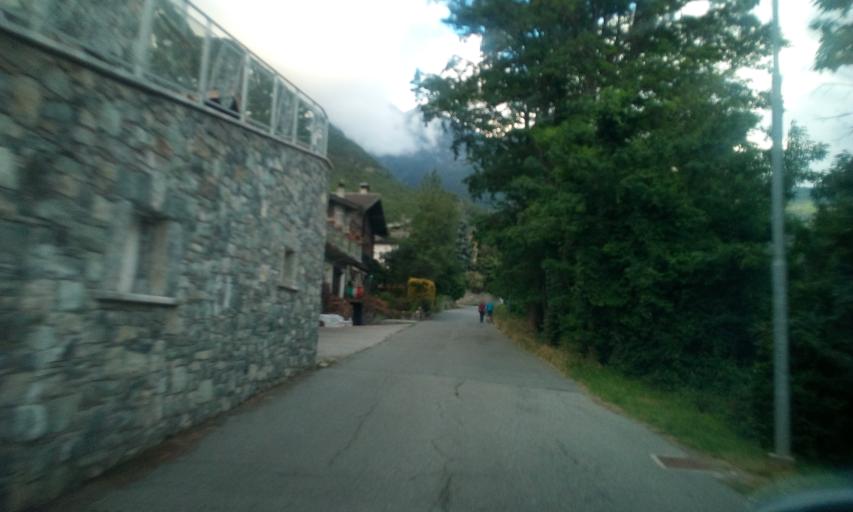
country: IT
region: Aosta Valley
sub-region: Valle d'Aosta
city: Chatillon
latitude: 45.7563
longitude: 7.6310
